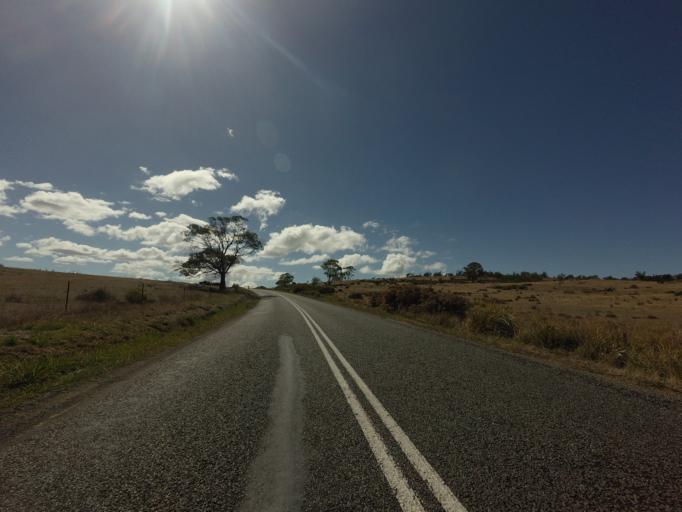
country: AU
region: Tasmania
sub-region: Break O'Day
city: St Helens
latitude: -41.9971
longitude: 148.0919
